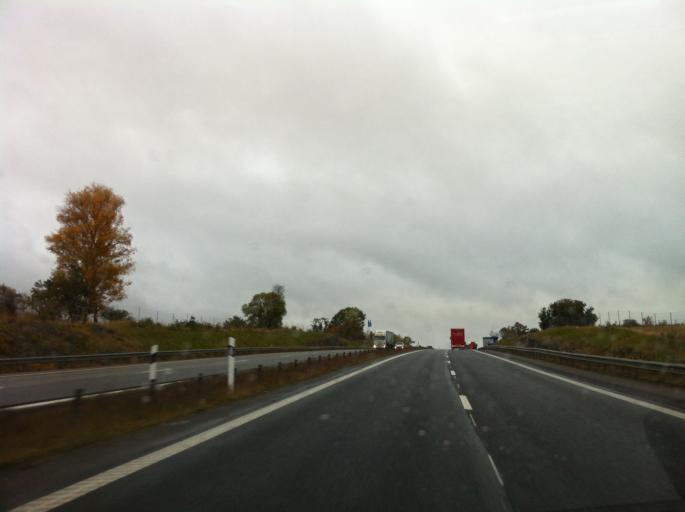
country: SE
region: Joenkoeping
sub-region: Jonkopings Kommun
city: Kaxholmen
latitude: 57.9320
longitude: 14.3290
